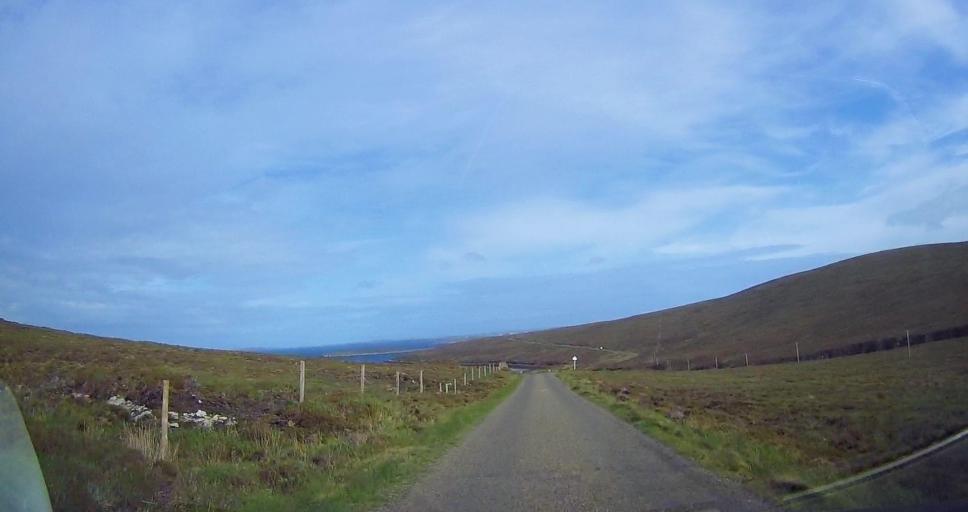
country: GB
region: Scotland
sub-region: Orkney Islands
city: Stromness
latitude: 58.8737
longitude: -3.2413
